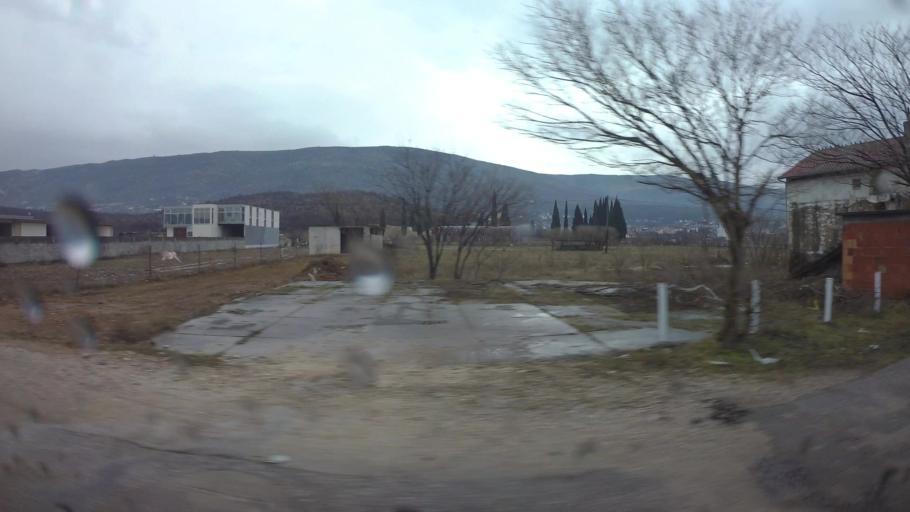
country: BA
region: Federation of Bosnia and Herzegovina
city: Rodoc
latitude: 43.2890
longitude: 17.8478
